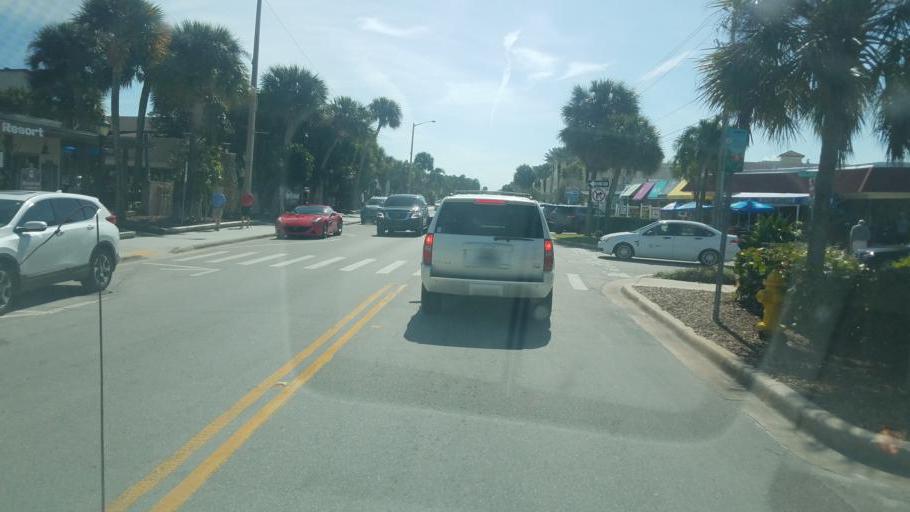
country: US
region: Florida
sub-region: Indian River County
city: Vero Beach
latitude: 27.6517
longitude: -80.3561
